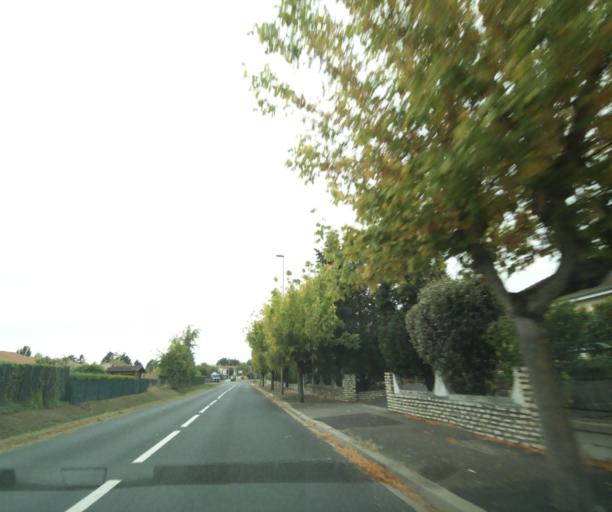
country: FR
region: Auvergne
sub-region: Departement du Puy-de-Dome
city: Gerzat
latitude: 45.8361
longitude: 3.1490
